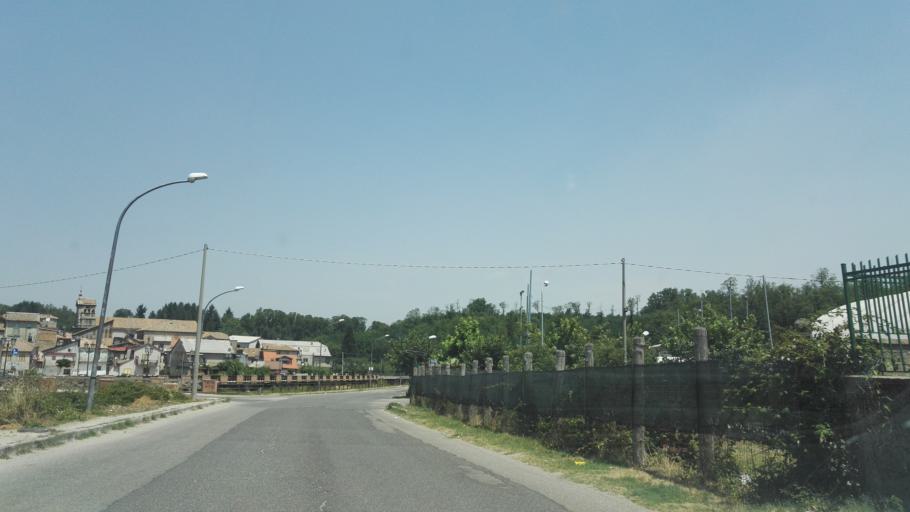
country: IT
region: Calabria
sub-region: Provincia di Vibo-Valentia
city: Serra San Bruno
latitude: 38.5774
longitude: 16.3326
